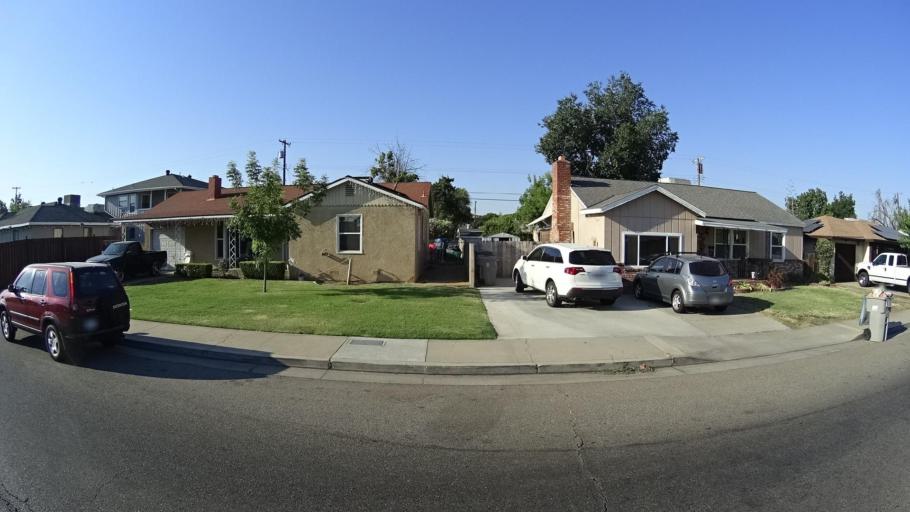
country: US
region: California
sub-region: Fresno County
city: Fresno
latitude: 36.7723
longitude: -119.7604
